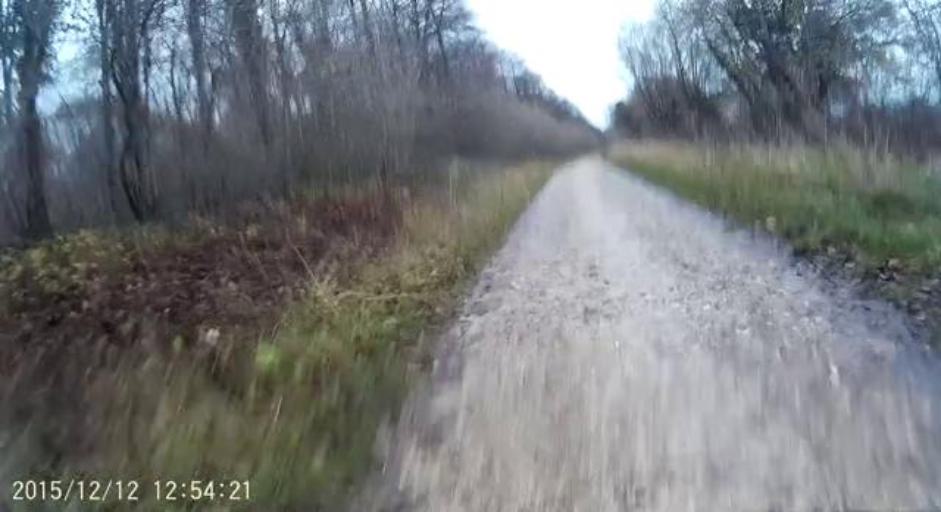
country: GB
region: England
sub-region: Hampshire
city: Petersfield
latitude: 50.9702
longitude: -0.9618
